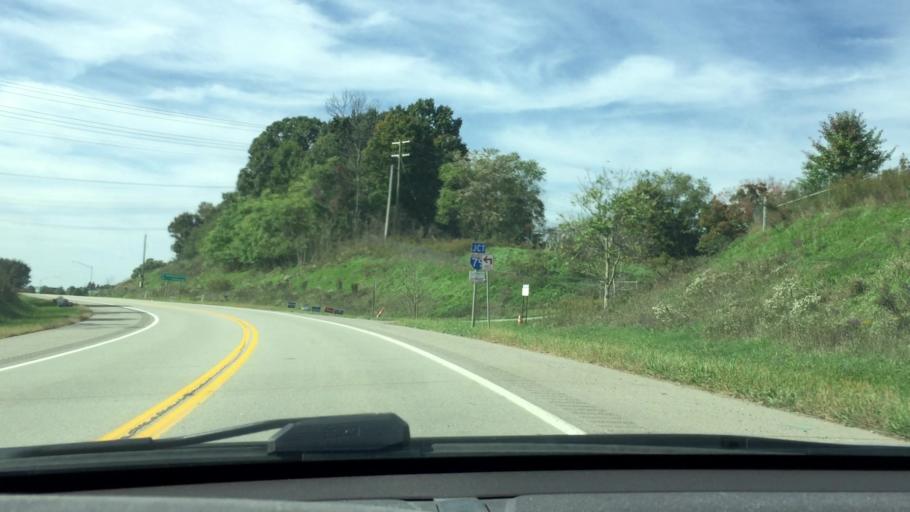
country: US
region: Pennsylvania
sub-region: Washington County
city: Cecil-Bishop
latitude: 40.2977
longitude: -80.1619
